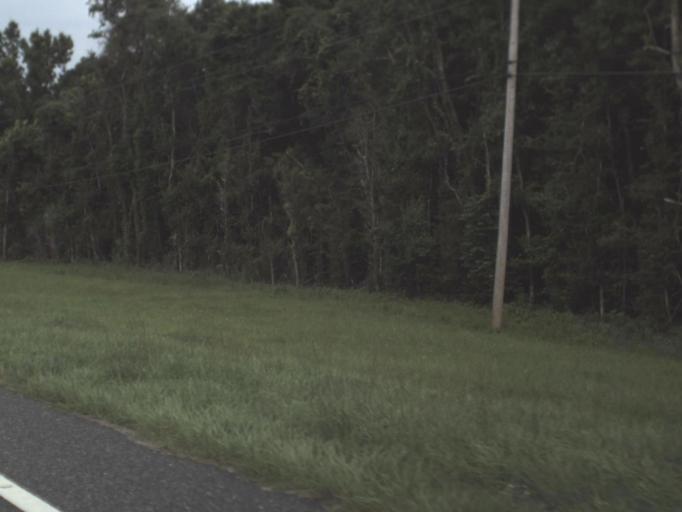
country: US
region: Florida
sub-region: Levy County
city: Williston Highlands
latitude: 29.2481
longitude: -82.7205
